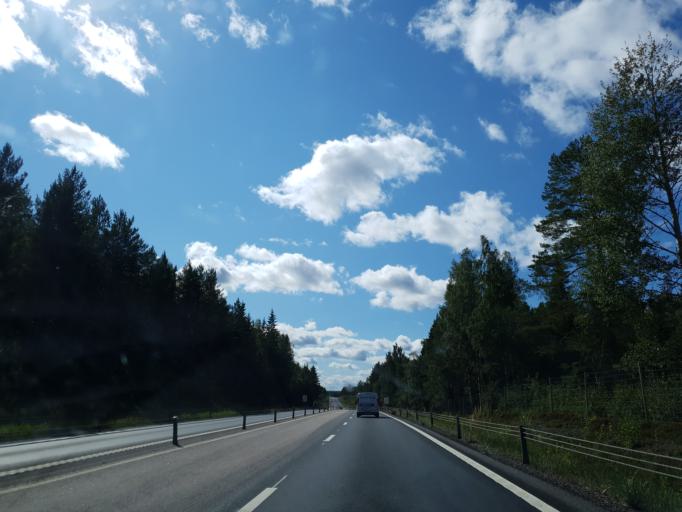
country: SE
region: Vaesterbotten
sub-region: Nordmalings Kommun
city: Nordmaling
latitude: 63.5146
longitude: 19.3628
